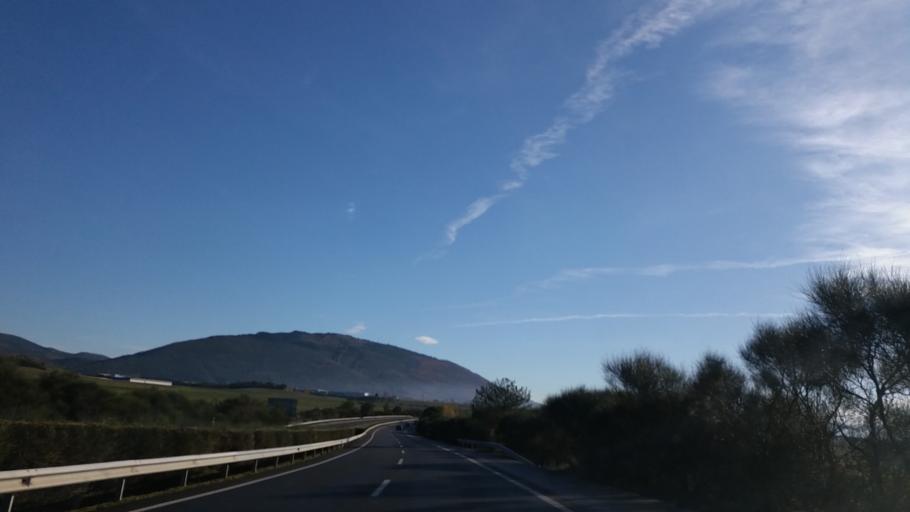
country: ES
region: Navarre
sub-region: Provincia de Navarra
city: Berriobeiti
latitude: 42.8551
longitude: -1.7262
